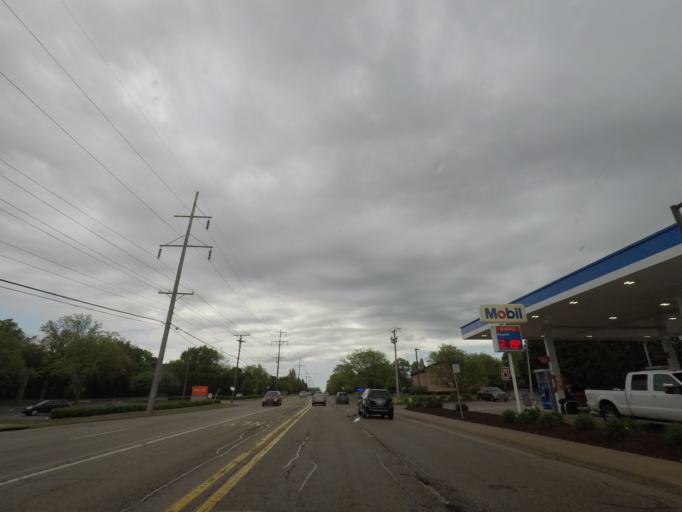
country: US
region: Illinois
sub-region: Winnebago County
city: Loves Park
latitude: 42.2867
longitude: -89.0291
